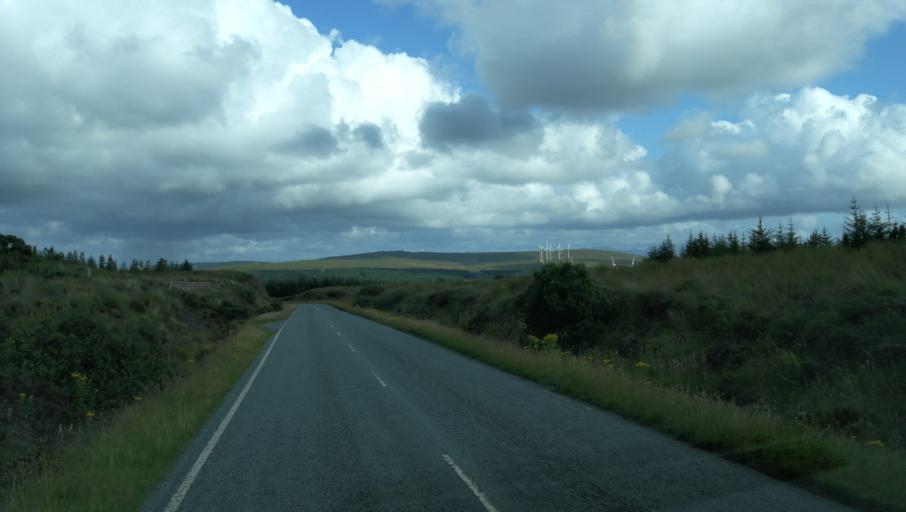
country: GB
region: Scotland
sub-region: Highland
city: Isle of Skye
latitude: 57.4644
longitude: -6.5063
